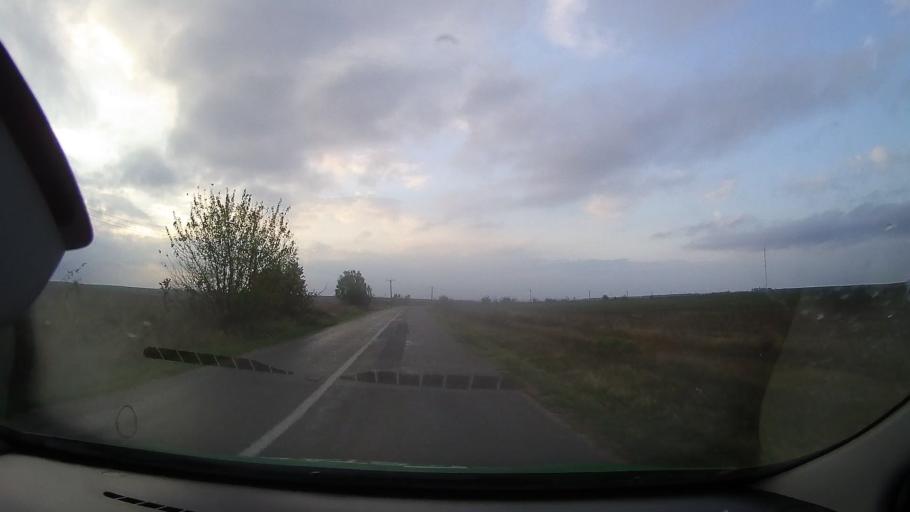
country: RO
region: Constanta
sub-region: Comuna Dobromir
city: Dobromir
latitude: 44.0348
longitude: 27.7621
